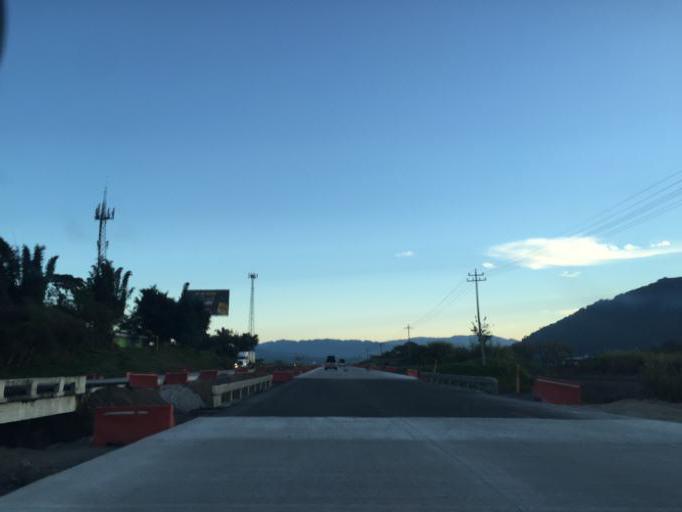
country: MX
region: Veracruz
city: Ixtac Zoquitlan
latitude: 18.8753
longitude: -97.0596
